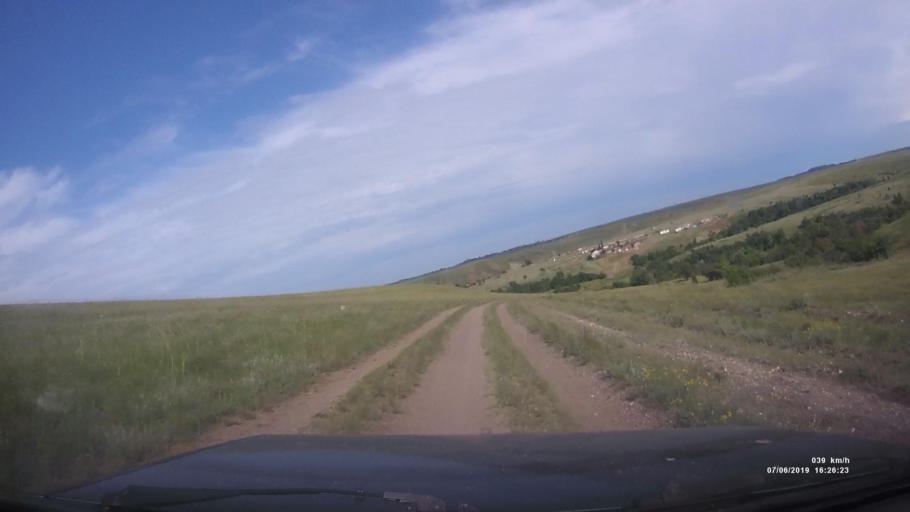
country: RU
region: Rostov
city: Kamensk-Shakhtinskiy
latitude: 48.2523
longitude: 40.3108
